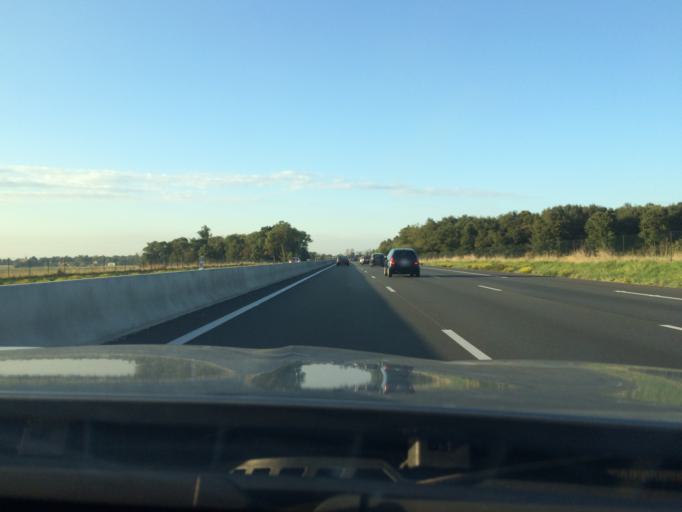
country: FR
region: Ile-de-France
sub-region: Departement de l'Essonne
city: Le Coudray-Montceaux
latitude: 48.5449
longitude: 2.4968
